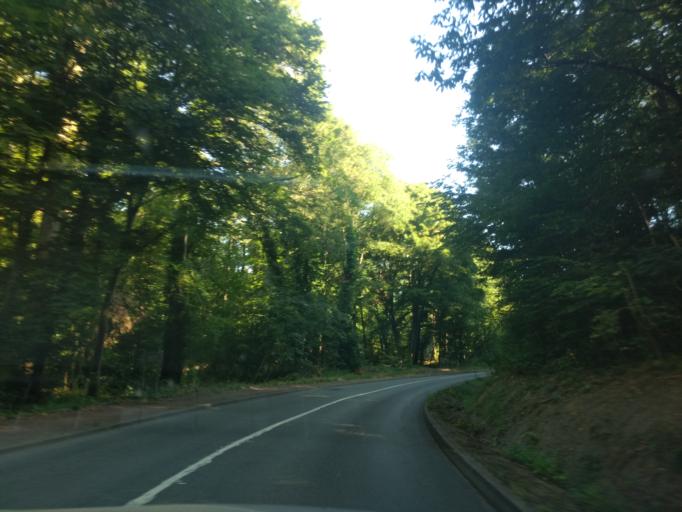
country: FR
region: Ile-de-France
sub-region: Departement des Yvelines
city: Jouy-en-Josas
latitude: 48.7756
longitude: 2.1711
